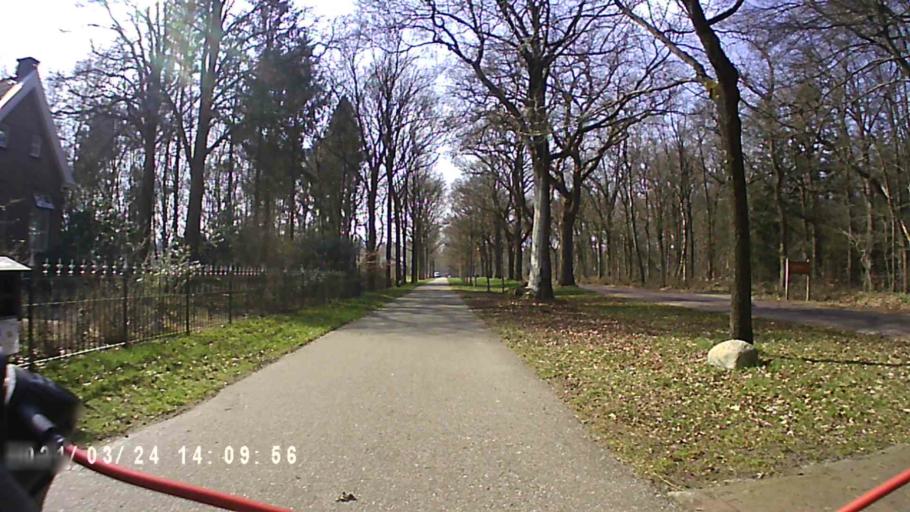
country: NL
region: Friesland
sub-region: Gemeente Smallingerland
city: Drachtstercompagnie
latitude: 53.0709
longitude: 6.2340
